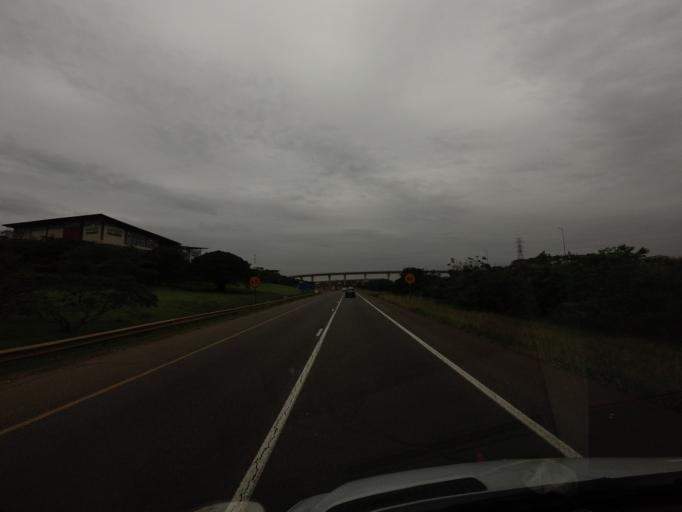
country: ZA
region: KwaZulu-Natal
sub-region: eThekwini Metropolitan Municipality
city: Durban
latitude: -29.7190
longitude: 31.0611
